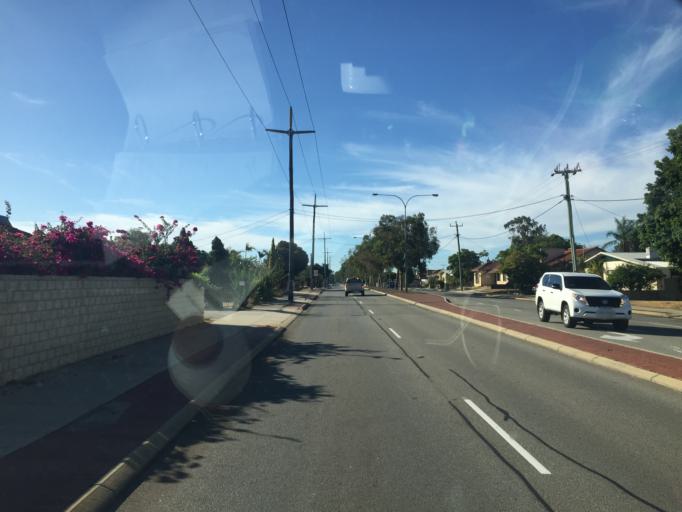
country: AU
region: Western Australia
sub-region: Belmont
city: Kewdale
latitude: -31.9682
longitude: 115.9429
